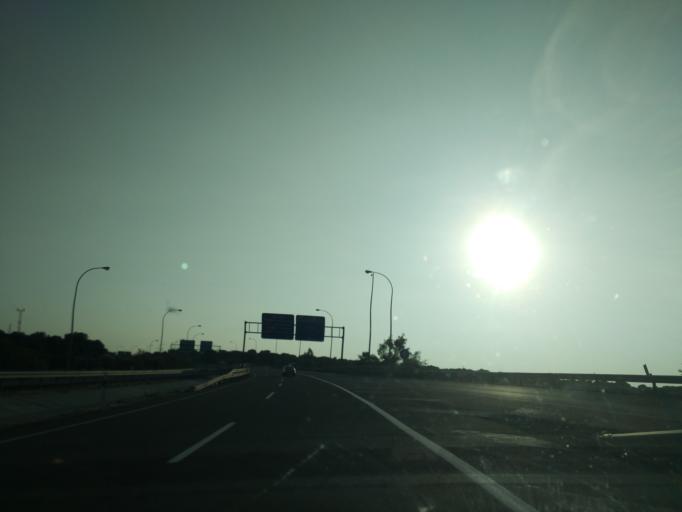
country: ES
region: Castille and Leon
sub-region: Provincia de Avila
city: Berrocalejo de Aragona
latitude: 40.6783
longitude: -4.6360
